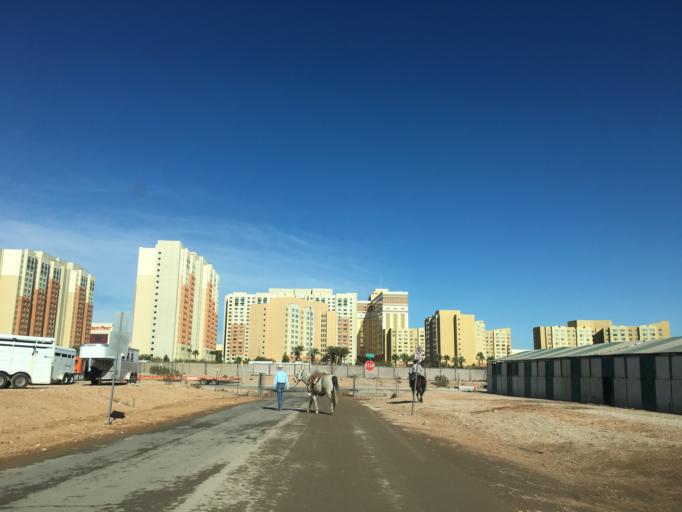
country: US
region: Nevada
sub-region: Clark County
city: Enterprise
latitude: 36.0058
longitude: -115.1769
